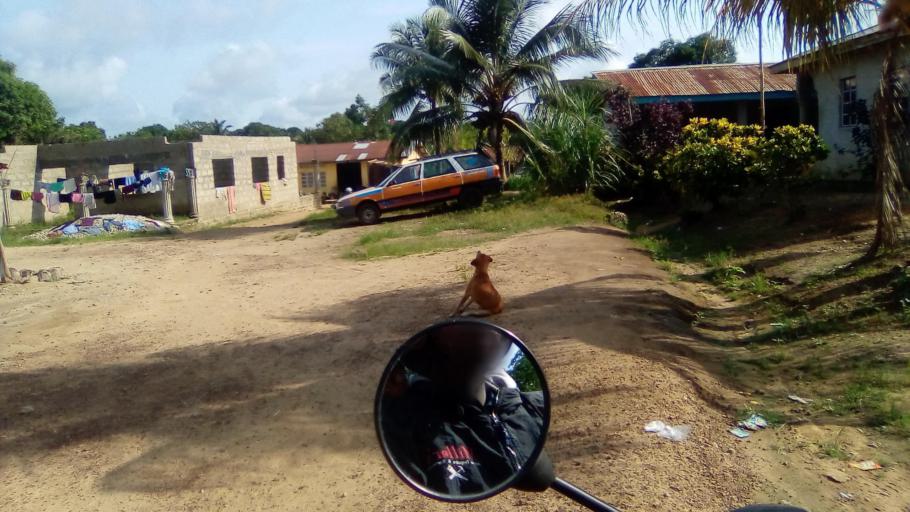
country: SL
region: Southern Province
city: Bo
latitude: 7.9563
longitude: -11.7617
